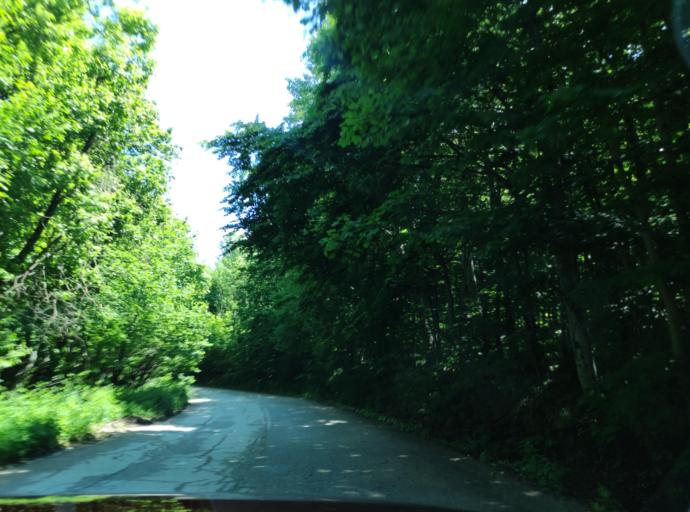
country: BG
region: Sofia-Capital
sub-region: Stolichna Obshtina
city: Sofia
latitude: 42.6342
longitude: 23.2417
